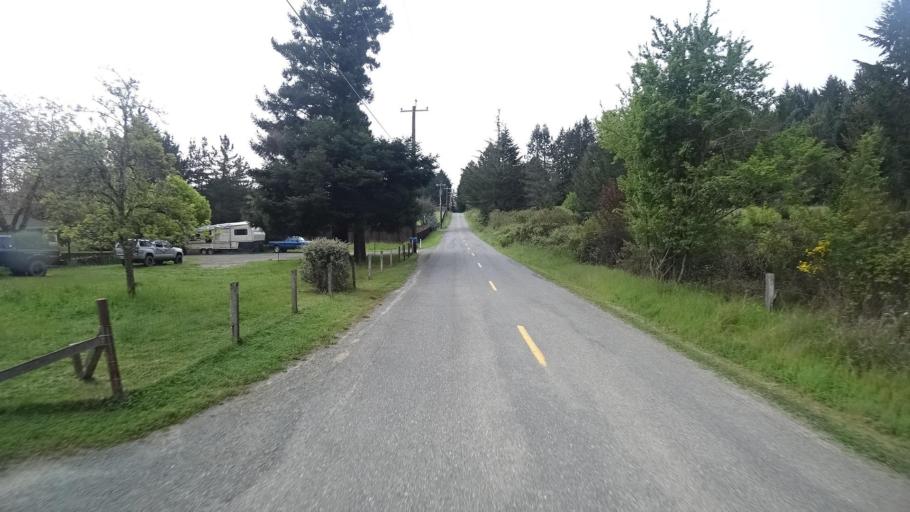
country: US
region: California
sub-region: Humboldt County
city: Redway
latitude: 40.2986
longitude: -123.8215
